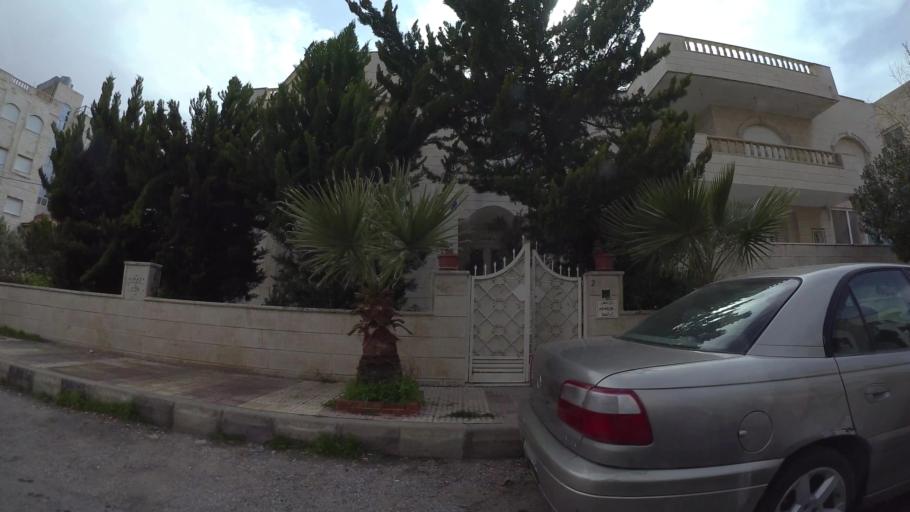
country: JO
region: Amman
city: Amman
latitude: 32.0022
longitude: 35.9397
